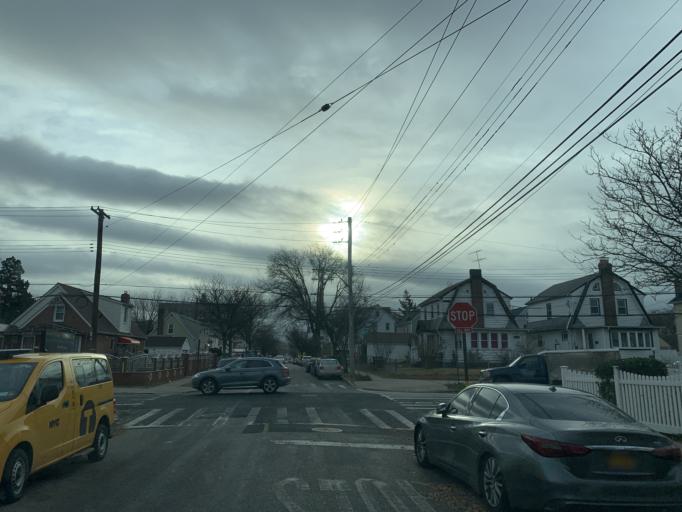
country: US
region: New York
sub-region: Queens County
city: Jamaica
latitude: 40.6894
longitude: -73.8023
